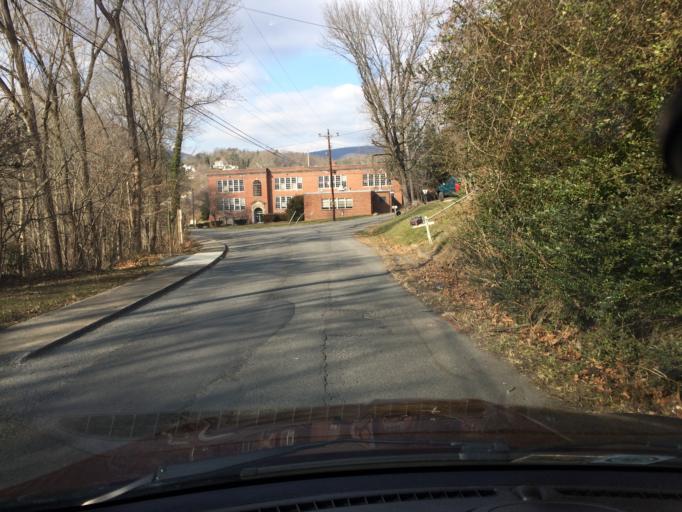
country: US
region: Virginia
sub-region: Alleghany County
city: Clifton Forge
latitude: 37.8211
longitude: -79.8238
